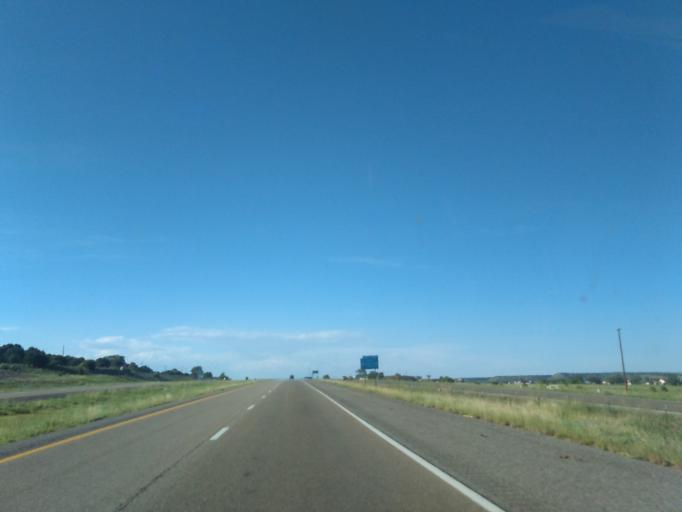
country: US
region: New Mexico
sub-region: San Miguel County
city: Las Vegas
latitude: 35.5391
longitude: -105.2288
